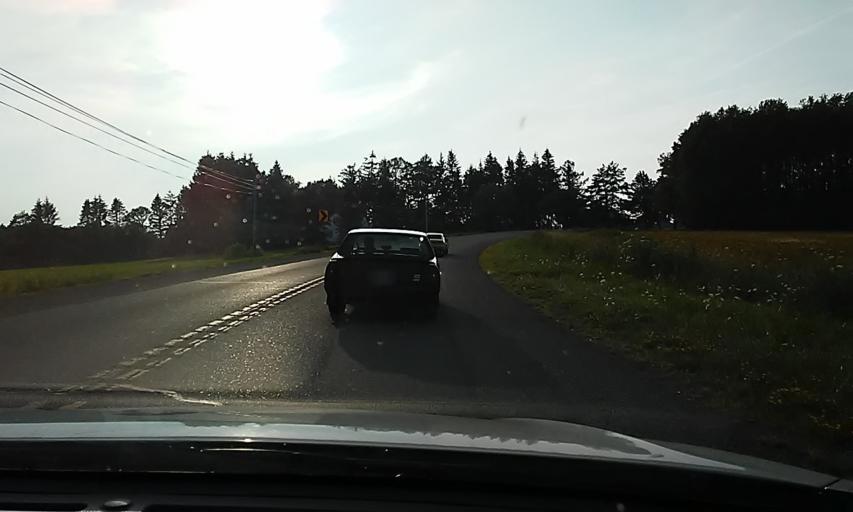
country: US
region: Pennsylvania
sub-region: McKean County
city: Kane
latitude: 41.6683
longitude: -78.7498
